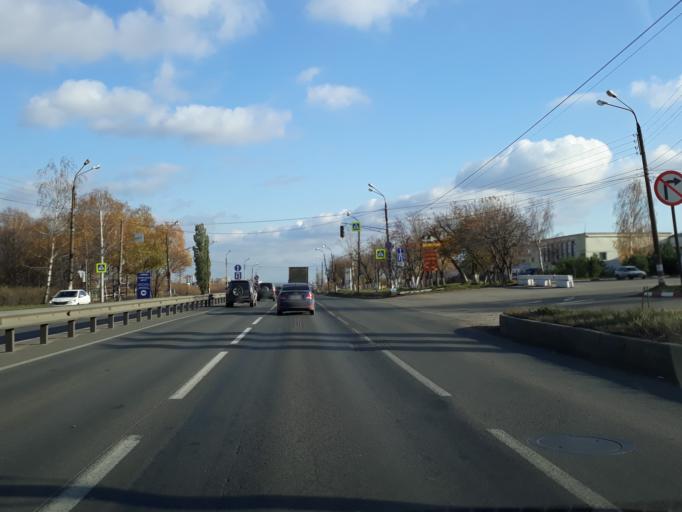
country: RU
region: Nizjnij Novgorod
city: Nizhniy Novgorod
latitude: 56.2401
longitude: 43.9902
